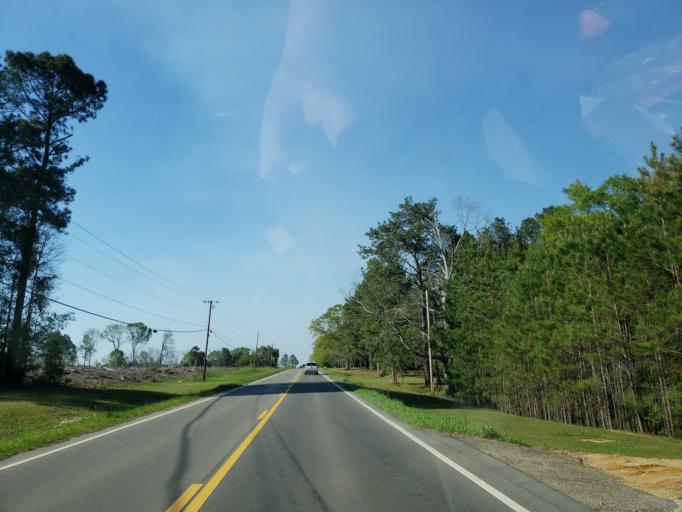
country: US
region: Mississippi
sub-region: Perry County
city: Richton
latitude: 31.3685
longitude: -88.9358
